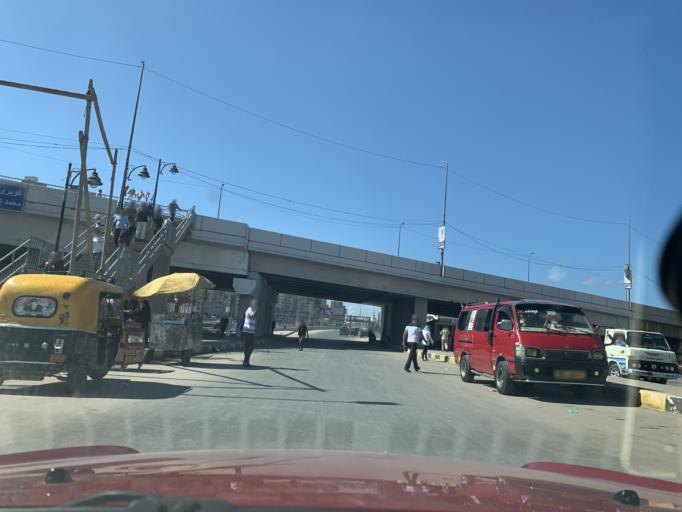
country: EG
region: Alexandria
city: Alexandria
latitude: 31.2188
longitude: 29.9945
